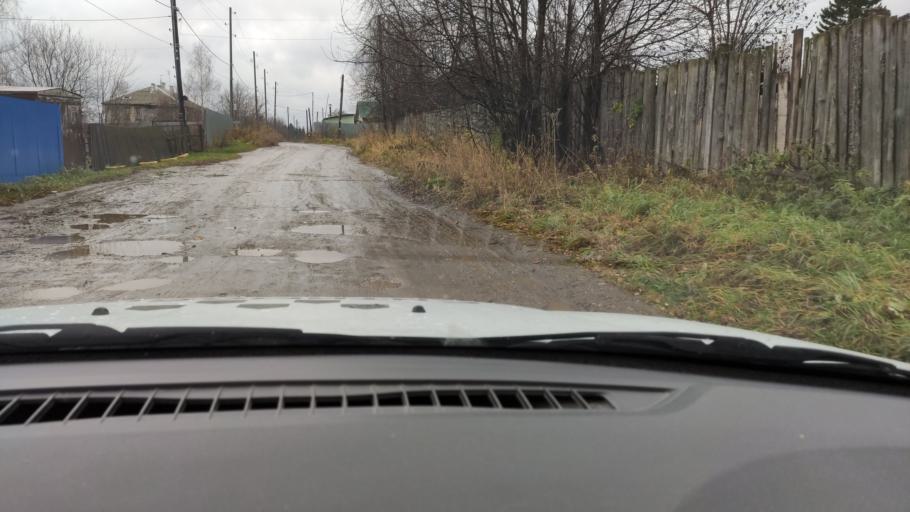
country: RU
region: Perm
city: Sylva
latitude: 58.0473
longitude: 56.7354
